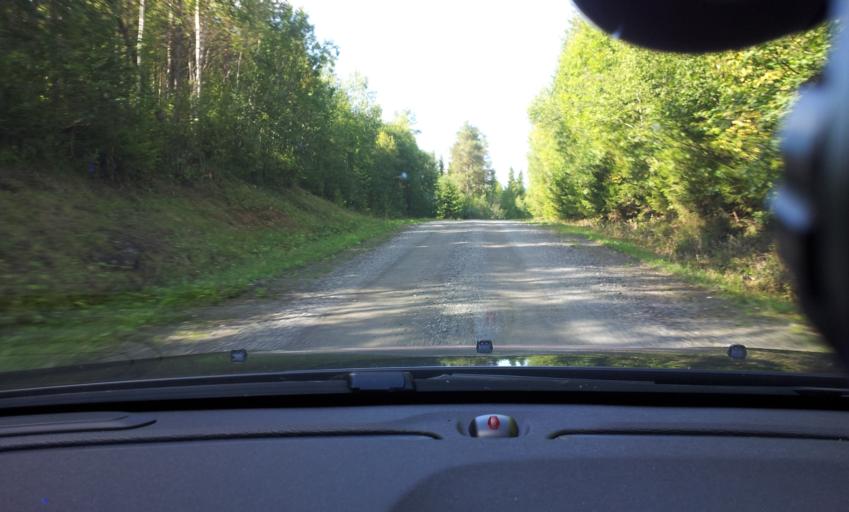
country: SE
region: Jaemtland
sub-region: Krokoms Kommun
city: Valla
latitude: 63.2589
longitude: 13.8176
